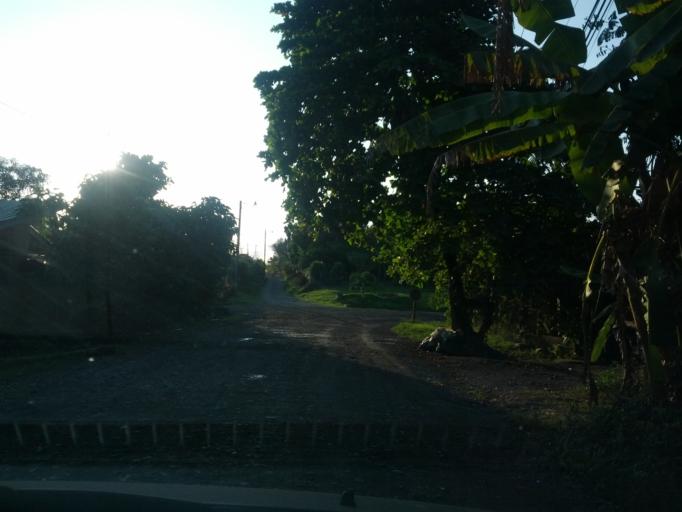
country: CR
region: Puntarenas
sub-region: Canton de Golfito
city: Golfito
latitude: 8.5360
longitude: -83.3035
